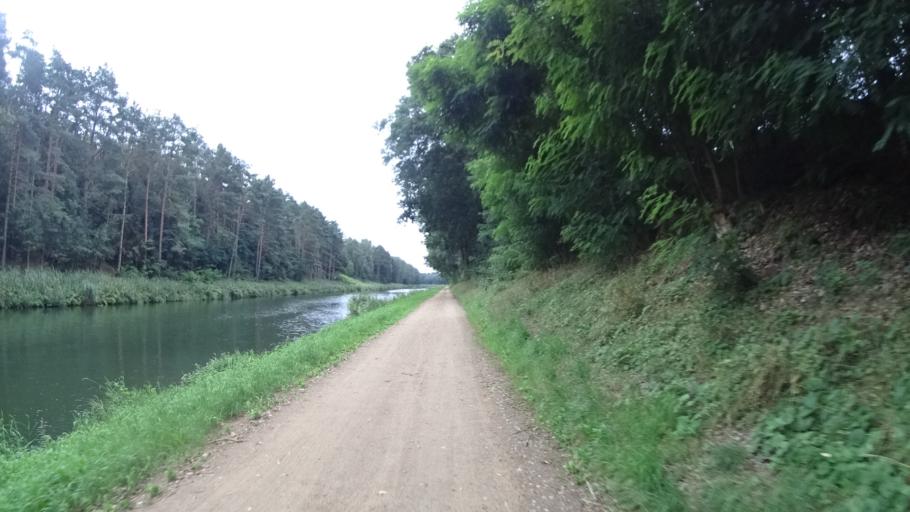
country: DE
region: Schleswig-Holstein
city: Grambek
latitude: 53.5952
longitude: 10.6662
